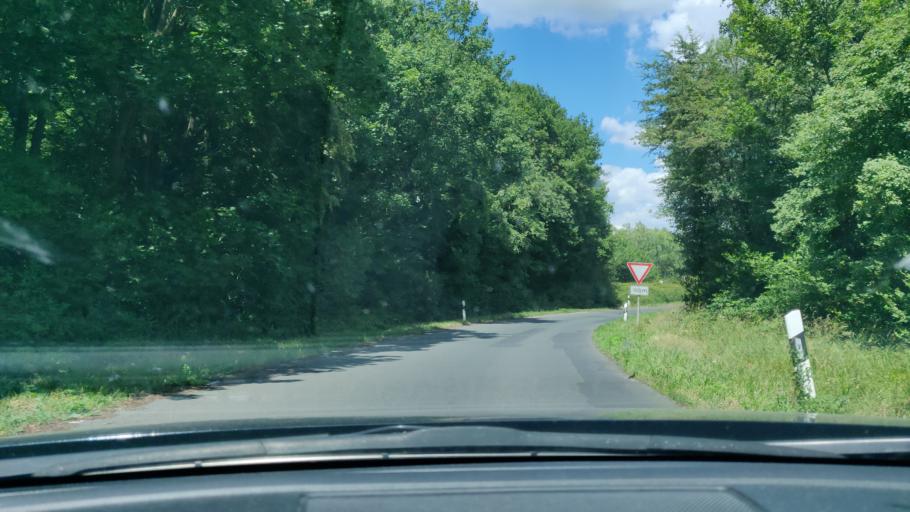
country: DE
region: Hesse
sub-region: Regierungsbezirk Kassel
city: Baunatal
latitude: 51.2650
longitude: 9.4316
